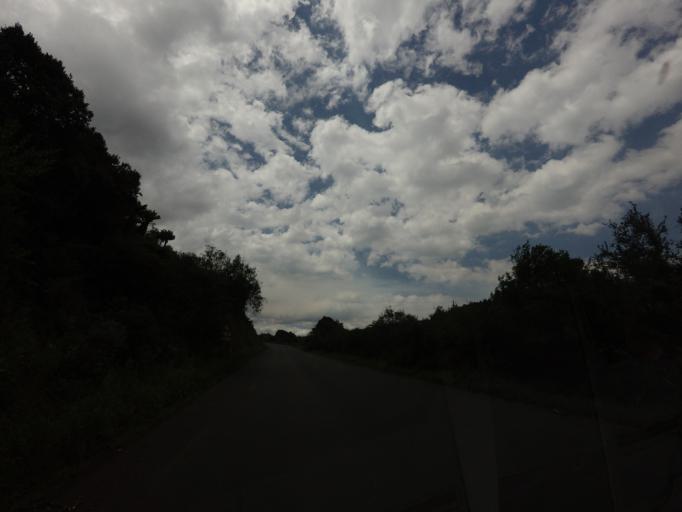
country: ZA
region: Mpumalanga
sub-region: Ehlanzeni District
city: Graksop
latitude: -24.9924
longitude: 30.8145
